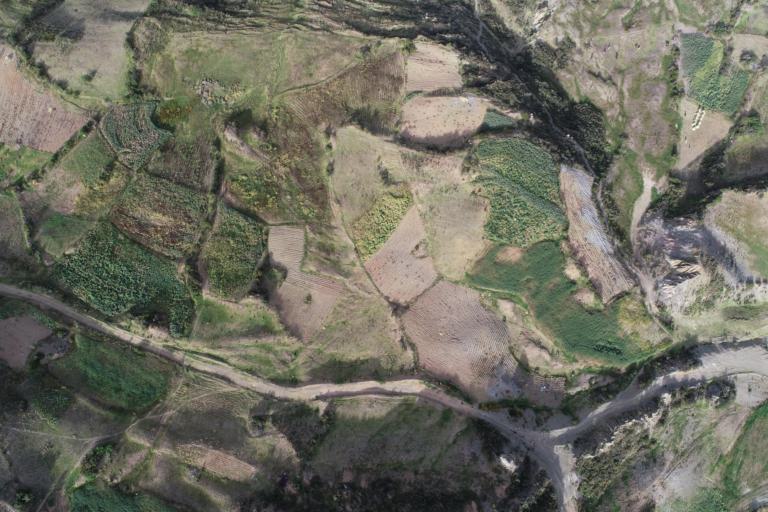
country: BO
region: La Paz
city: La Paz
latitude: -16.5497
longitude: -67.9978
